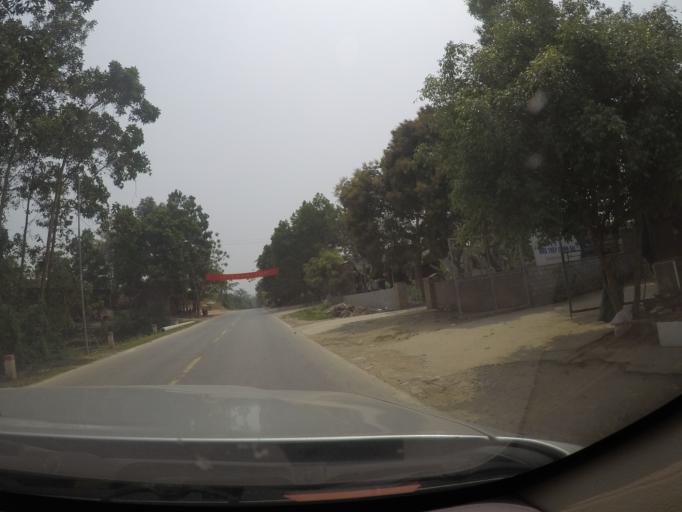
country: VN
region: Thanh Hoa
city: Thi Tran Yen Cat
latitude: 19.6951
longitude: 105.4532
